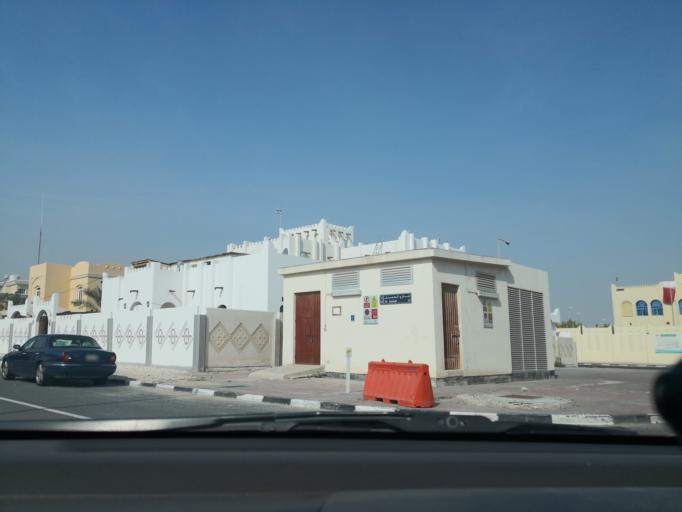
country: QA
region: Baladiyat ad Dawhah
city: Doha
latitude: 25.3279
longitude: 51.5114
